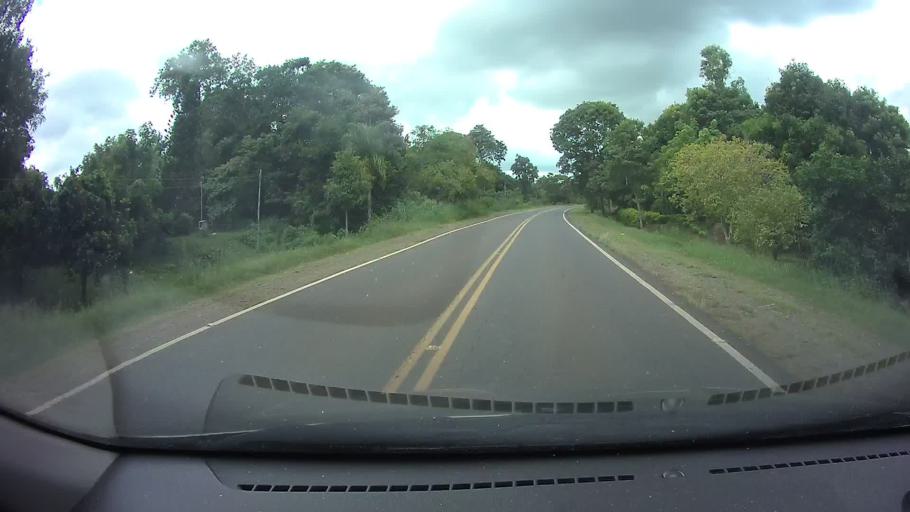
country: PY
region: Paraguari
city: Acahay
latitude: -25.9130
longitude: -57.0627
